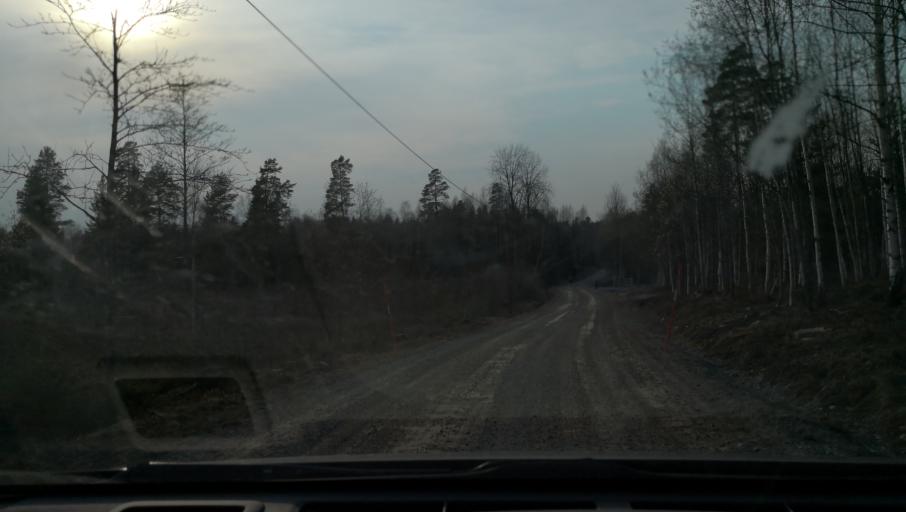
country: SE
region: OErebro
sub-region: Lindesbergs Kommun
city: Frovi
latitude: 59.3487
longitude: 15.3491
